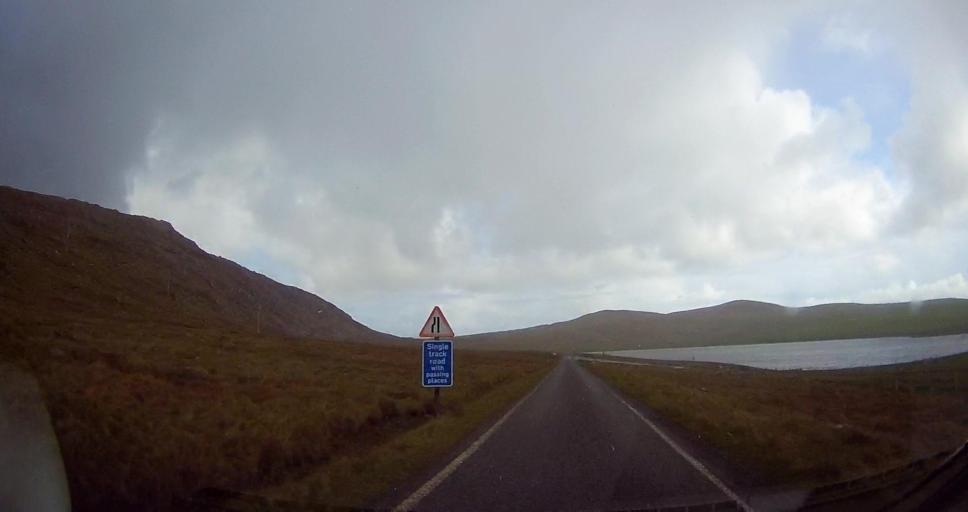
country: GB
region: Scotland
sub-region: Shetland Islands
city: Lerwick
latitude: 60.5467
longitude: -1.3416
